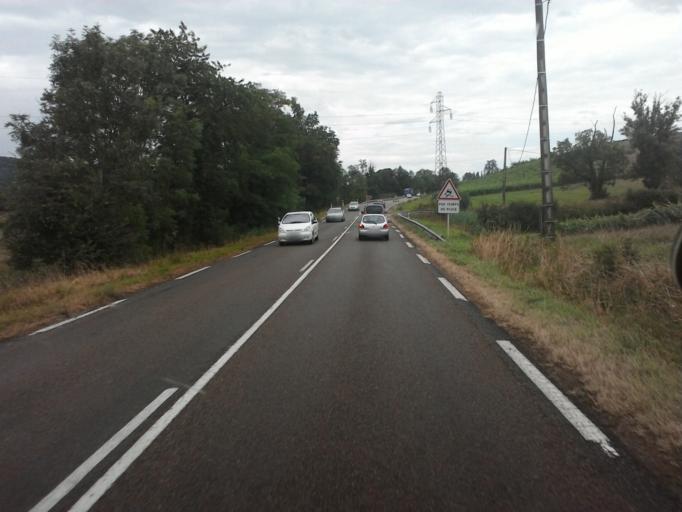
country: FR
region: Franche-Comte
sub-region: Departement du Jura
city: Arbois
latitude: 46.8881
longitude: 5.7291
